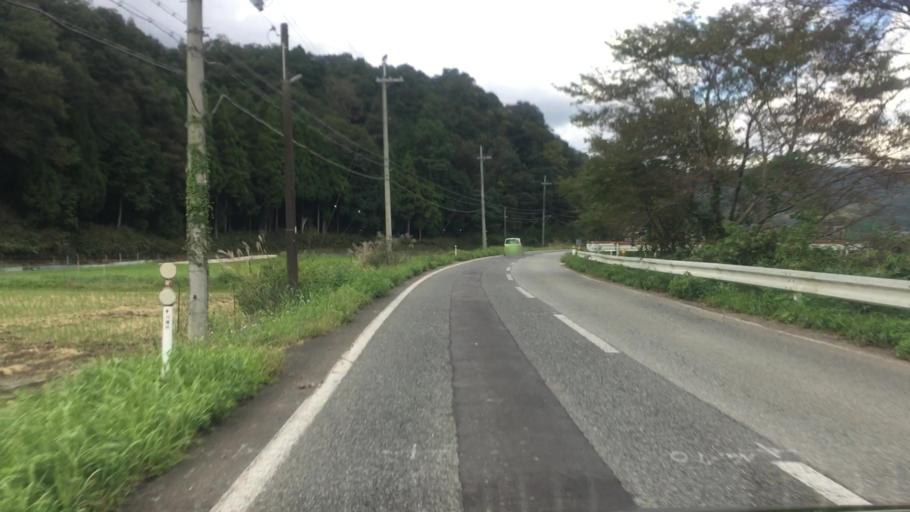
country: JP
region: Hyogo
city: Toyooka
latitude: 35.4445
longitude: 134.7300
